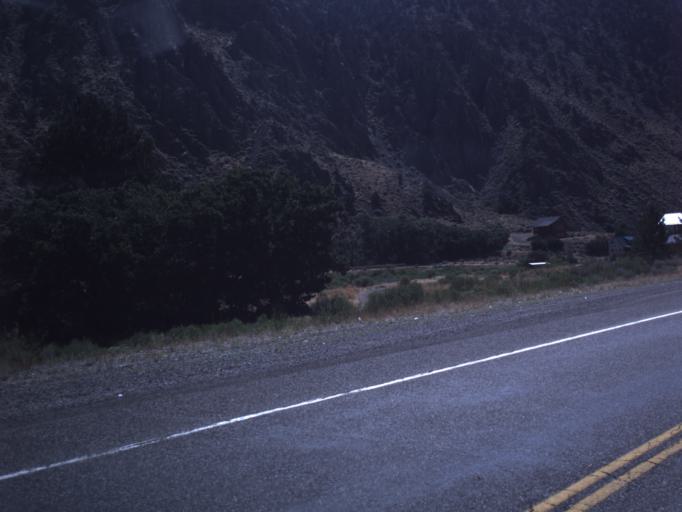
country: US
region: Utah
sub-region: Sevier County
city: Monroe
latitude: 38.5113
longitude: -112.2613
